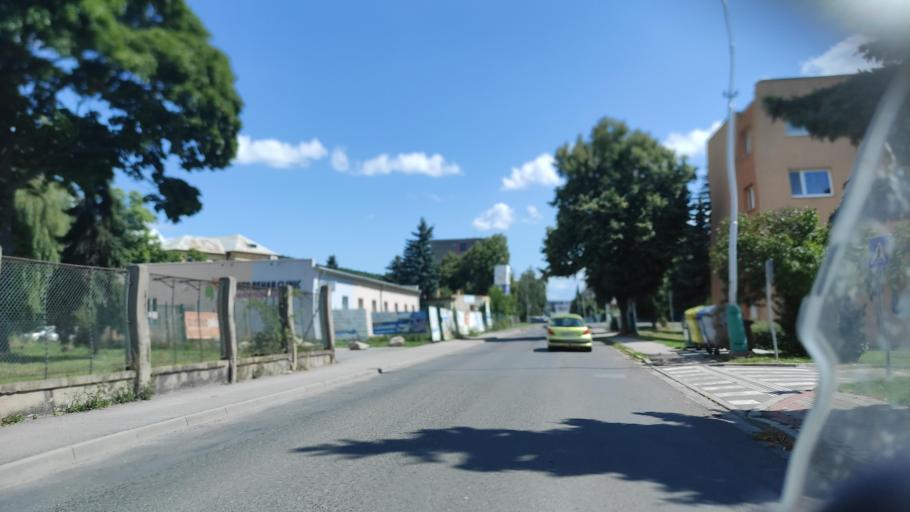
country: SK
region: Zilinsky
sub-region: Okres Liptovsky Mikulas
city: Liptovsky Mikulas
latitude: 49.0831
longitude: 19.6225
